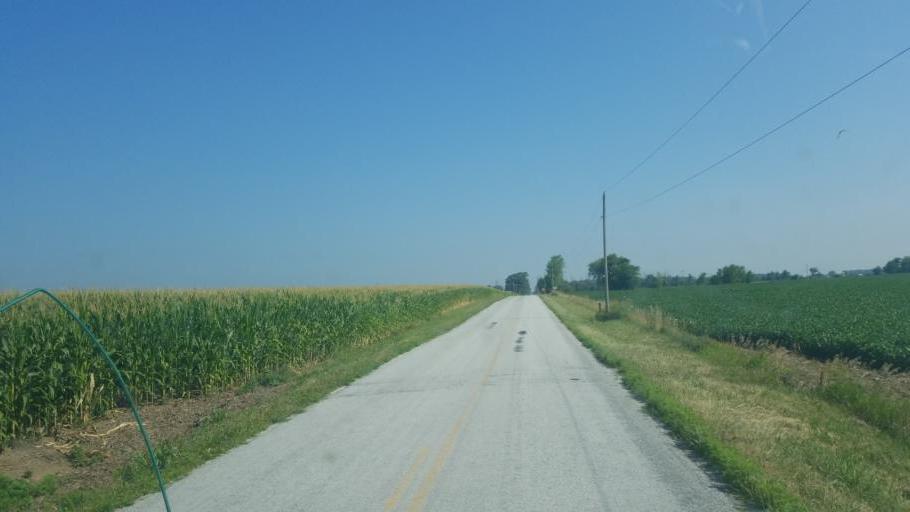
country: US
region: Ohio
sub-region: Hardin County
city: Kenton
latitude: 40.6677
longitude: -83.5380
